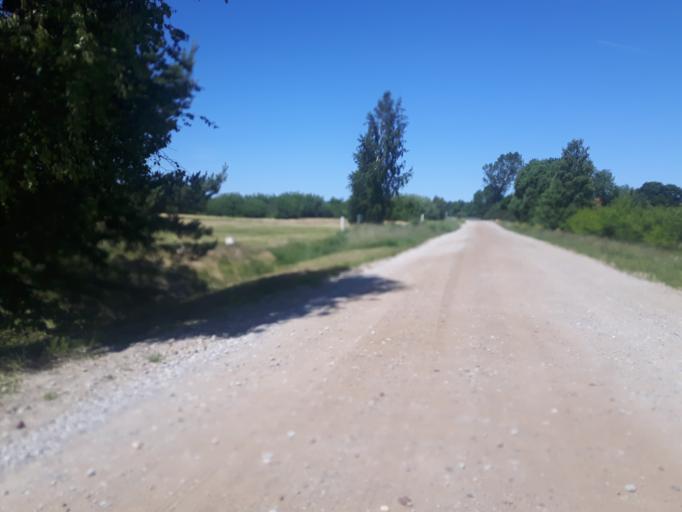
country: LV
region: Grobina
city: Grobina
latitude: 56.5307
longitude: 21.1299
